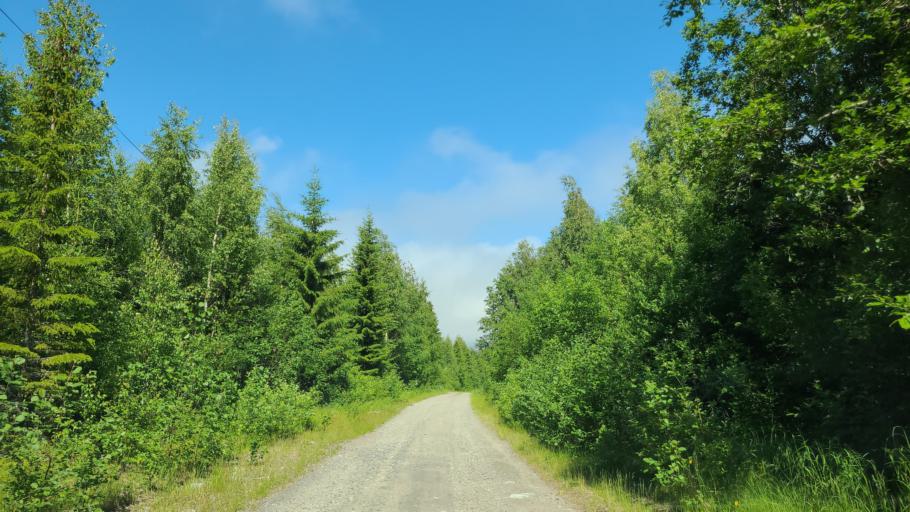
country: SE
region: Vaesternorrland
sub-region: OErnskoeldsviks Kommun
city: Husum
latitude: 63.4494
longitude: 19.2372
